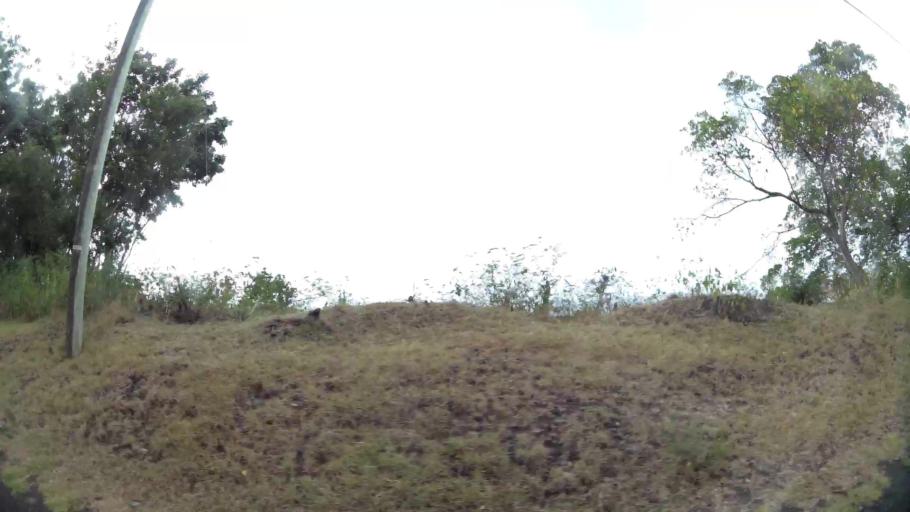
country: KN
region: Saint Thomas Lowland
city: Cotton Ground
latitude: 17.1955
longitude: -62.6141
